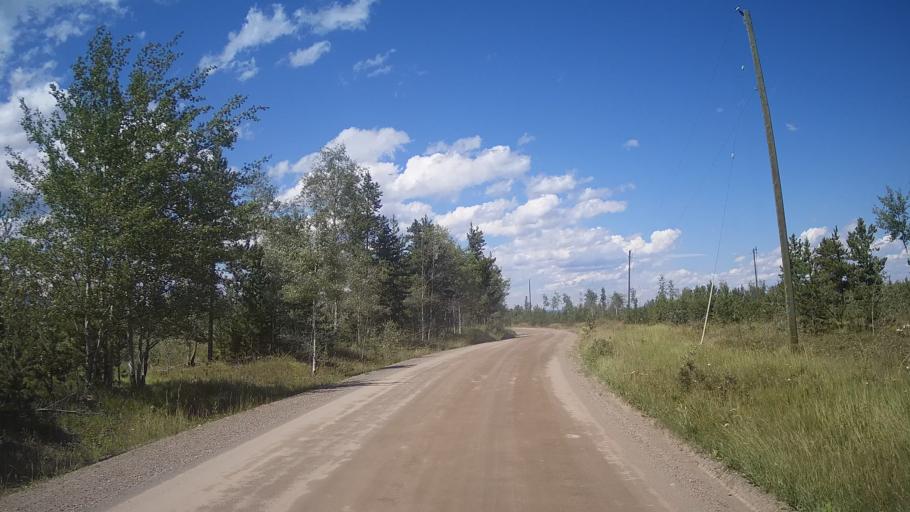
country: CA
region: British Columbia
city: Cache Creek
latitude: 51.2525
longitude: -121.6737
